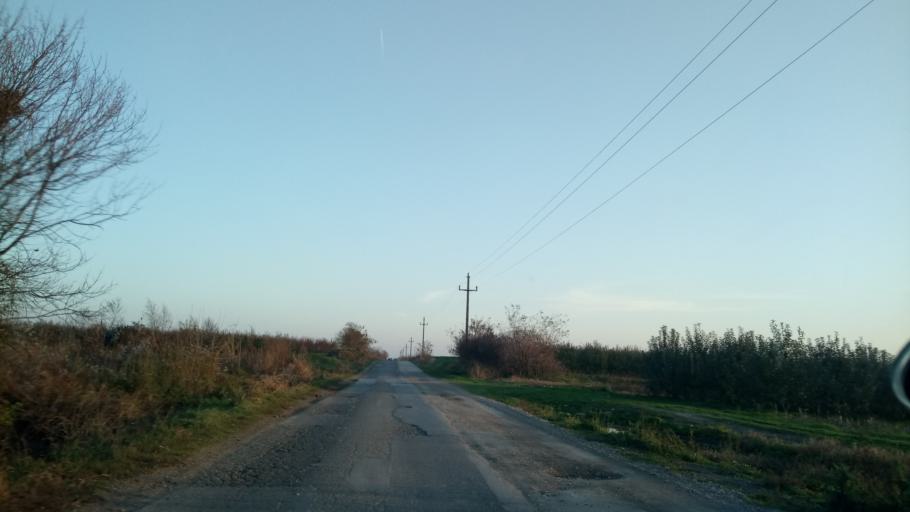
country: RS
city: Novi Slankamen
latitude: 45.1261
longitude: 20.2607
